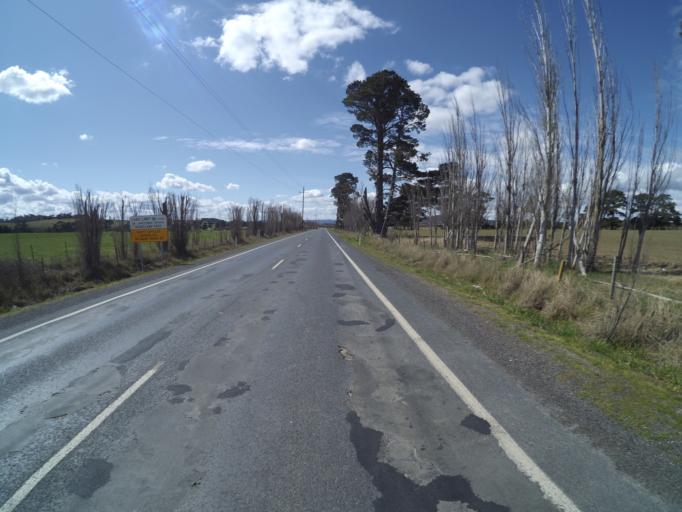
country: AU
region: New South Wales
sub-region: Goulburn Mulwaree
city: Goulburn
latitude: -34.7870
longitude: 149.7025
